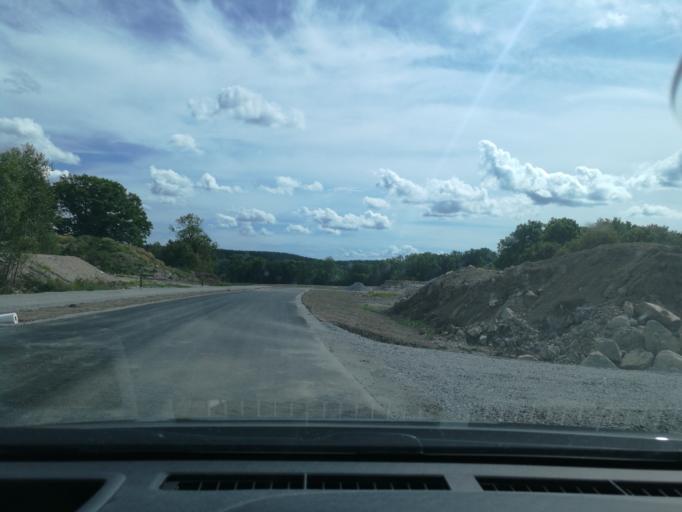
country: SE
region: Stockholm
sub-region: Sigtuna Kommun
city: Marsta
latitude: 59.6063
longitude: 17.8030
